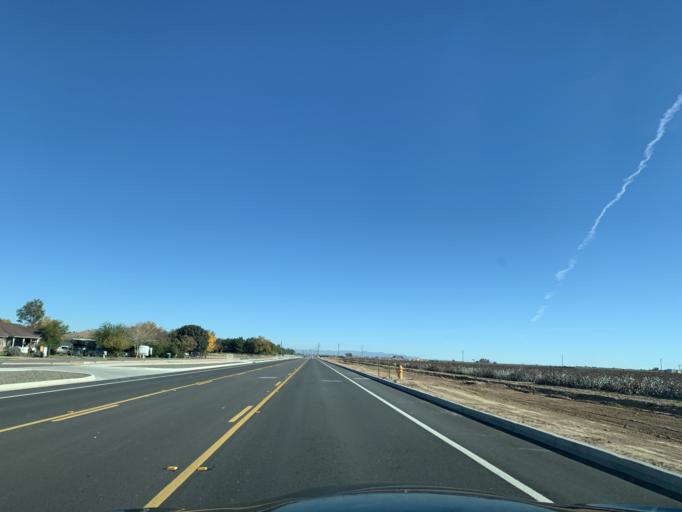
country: US
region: Arizona
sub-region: Maricopa County
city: Queen Creek
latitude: 33.2195
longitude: -111.6046
